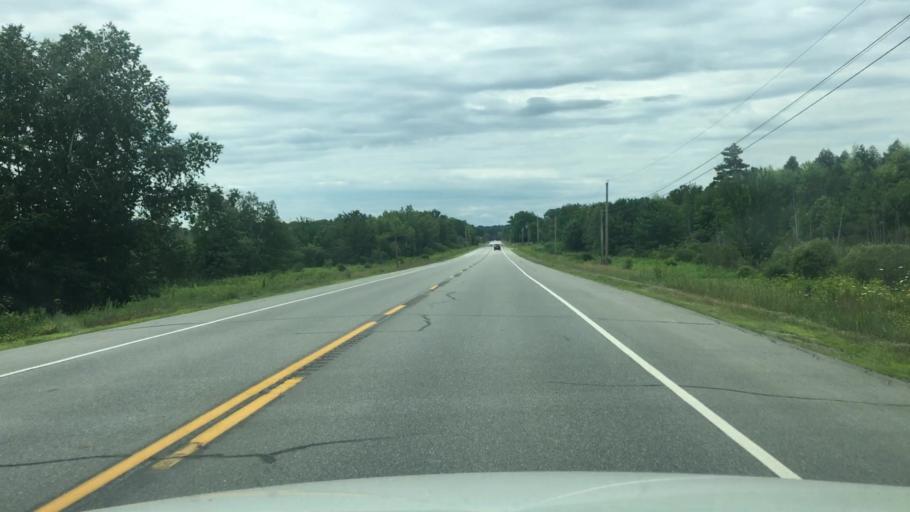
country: US
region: Maine
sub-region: Kennebec County
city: Windsor
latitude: 44.3918
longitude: -69.5802
